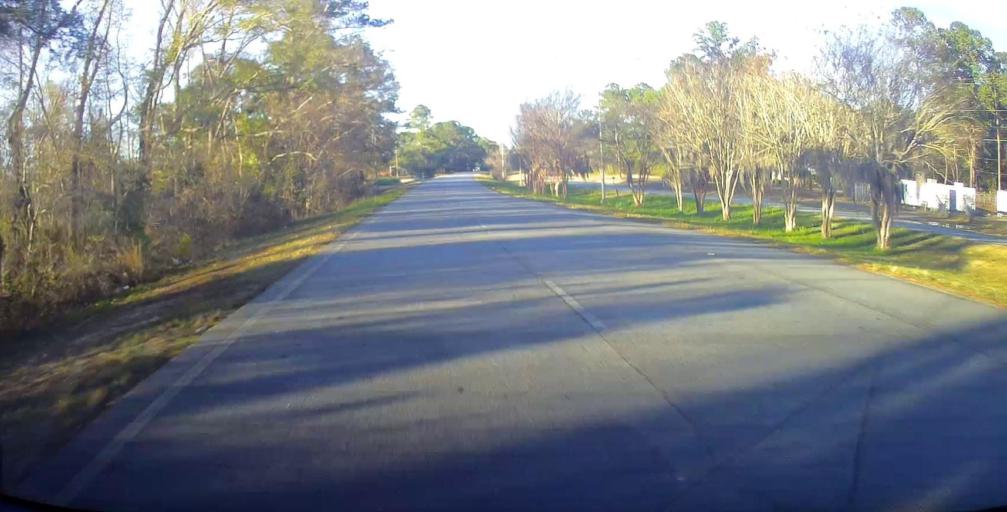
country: US
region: Georgia
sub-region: Dougherty County
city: Albany
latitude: 31.5580
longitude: -84.2252
